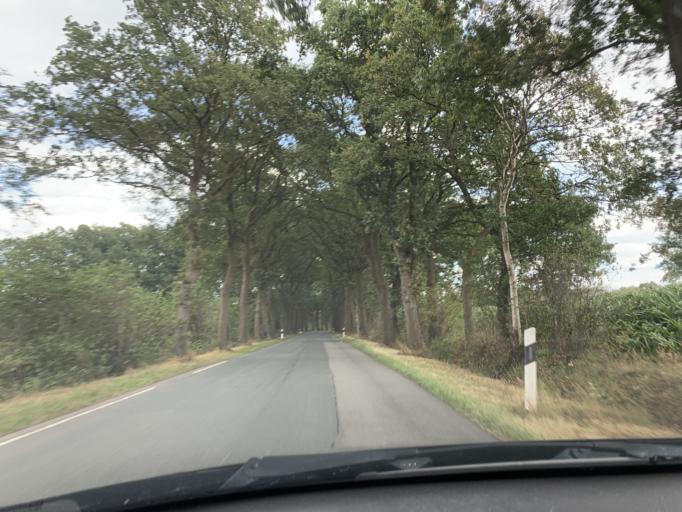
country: DE
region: Lower Saxony
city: Apen
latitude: 53.2227
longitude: 7.8523
